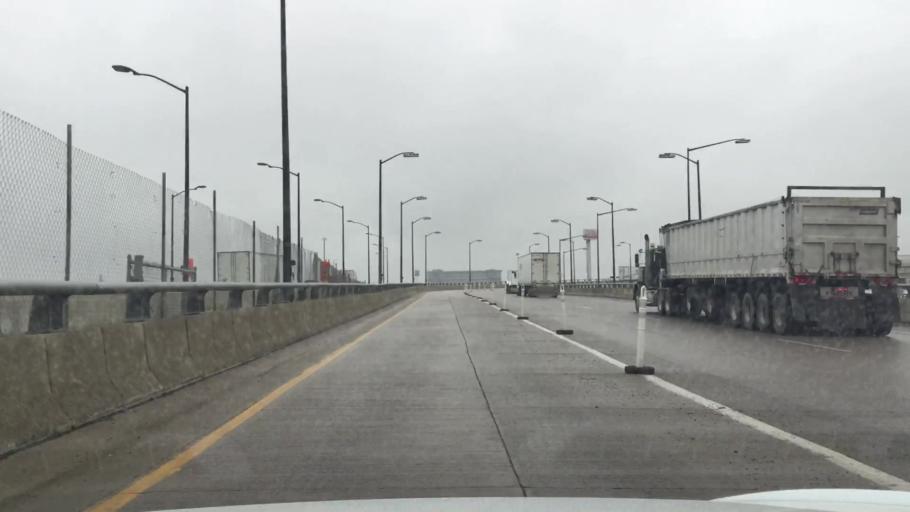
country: US
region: Michigan
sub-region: Wayne County
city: Detroit
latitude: 42.3171
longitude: -83.0821
